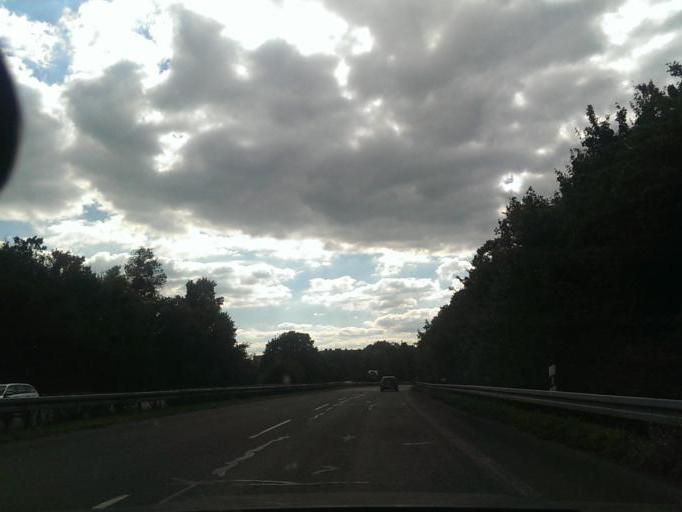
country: DE
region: Baden-Wuerttemberg
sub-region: Karlsruhe Region
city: Karlsruhe
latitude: 49.0058
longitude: 8.4669
